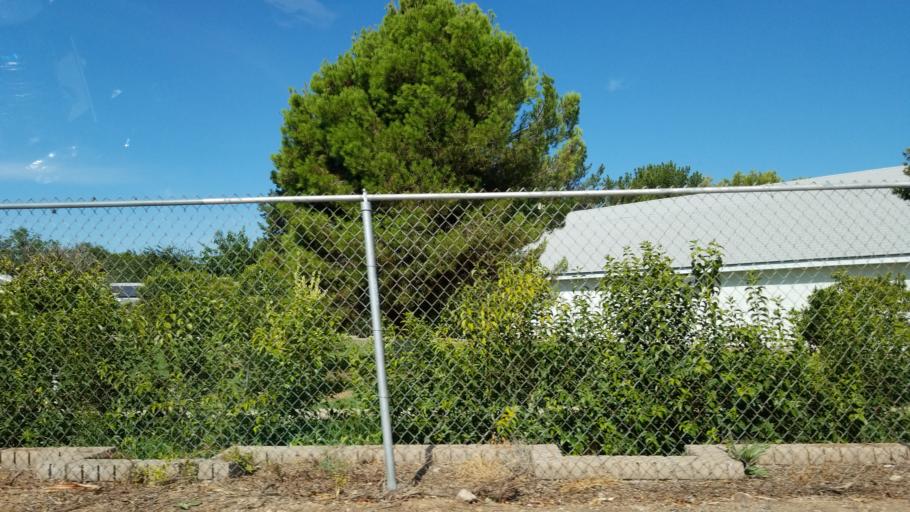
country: US
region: Arizona
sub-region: Maricopa County
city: Glendale
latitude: 33.6259
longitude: -112.1513
